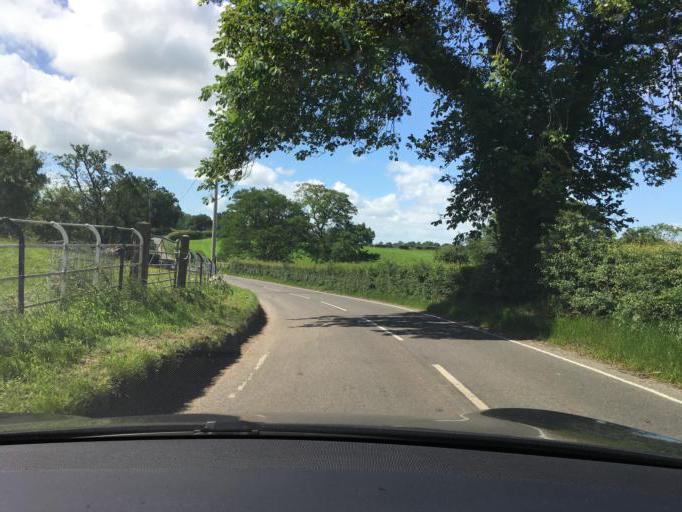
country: GB
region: England
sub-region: Cheshire East
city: Mobberley
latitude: 53.2967
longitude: -2.3048
